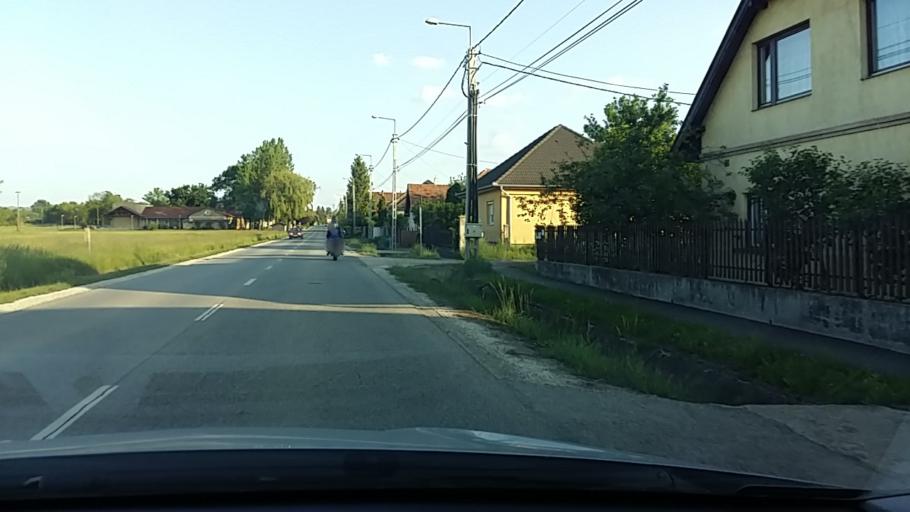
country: HU
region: Pest
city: Orbottyan
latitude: 47.7156
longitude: 19.2329
